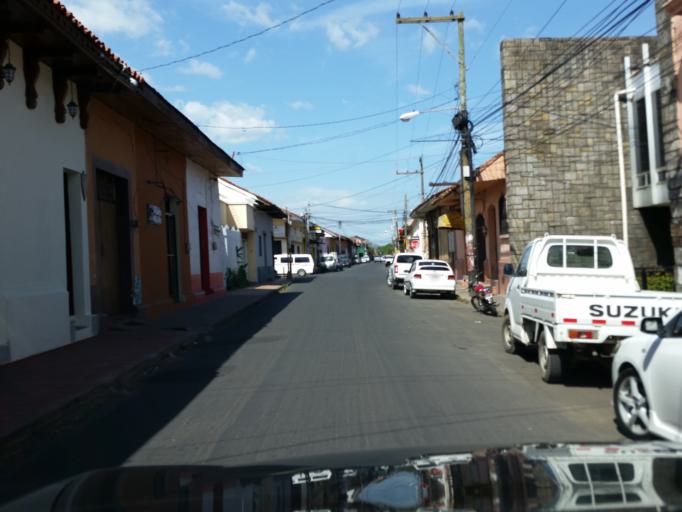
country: NI
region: Leon
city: Leon
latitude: 12.4377
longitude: -86.8752
